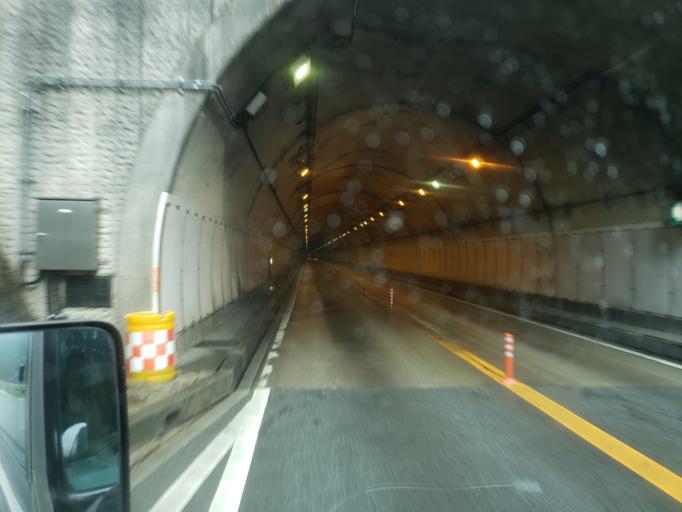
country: JP
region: Hyogo
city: Nishiwaki
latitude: 35.1511
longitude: 134.7865
